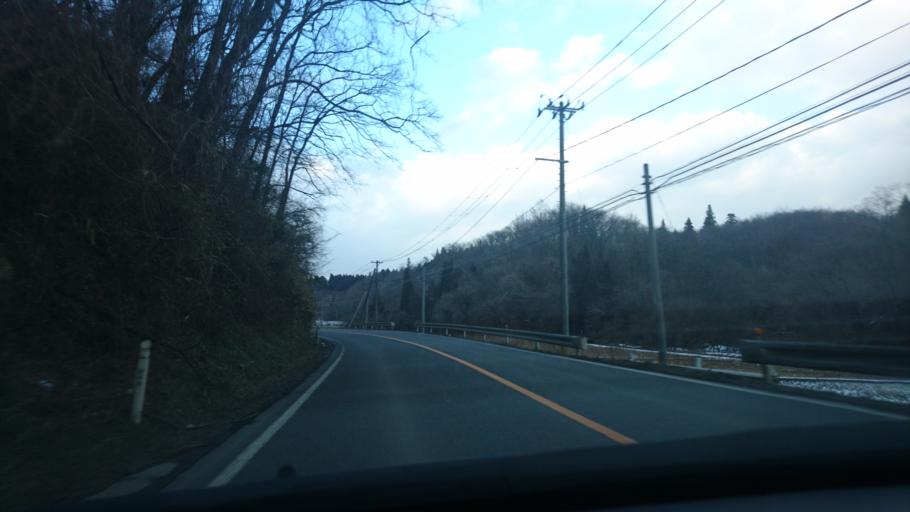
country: JP
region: Iwate
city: Ichinoseki
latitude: 38.9847
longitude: 141.3319
